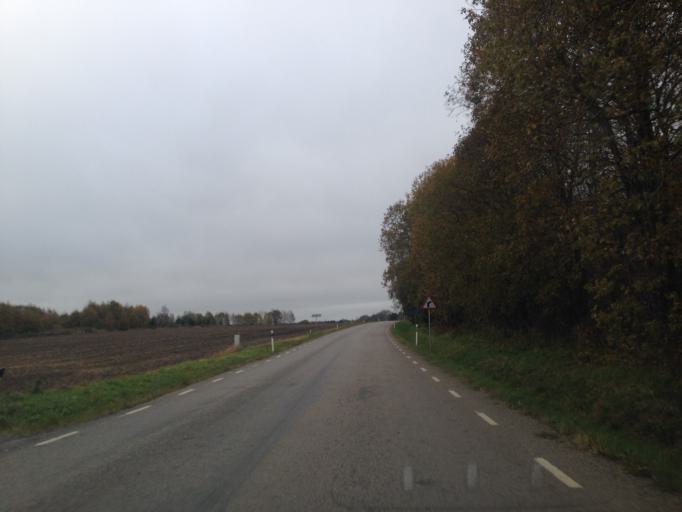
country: EE
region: Harju
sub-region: Saue linn
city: Saue
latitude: 59.3628
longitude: 24.5507
